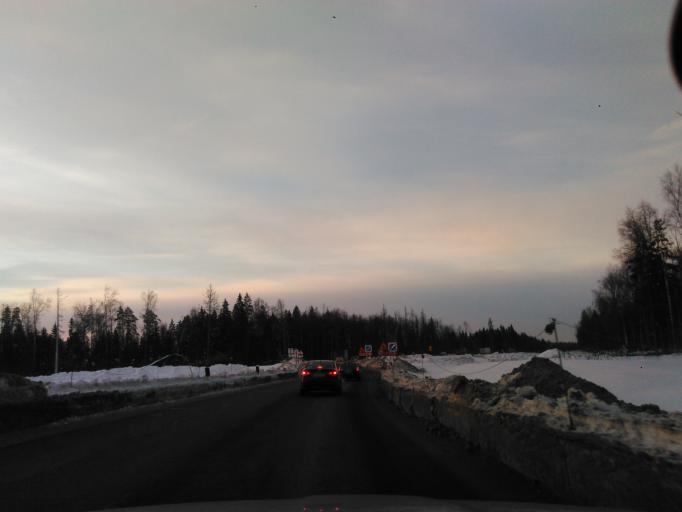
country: RU
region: Moskovskaya
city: Povarovo
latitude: 56.0034
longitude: 37.0249
